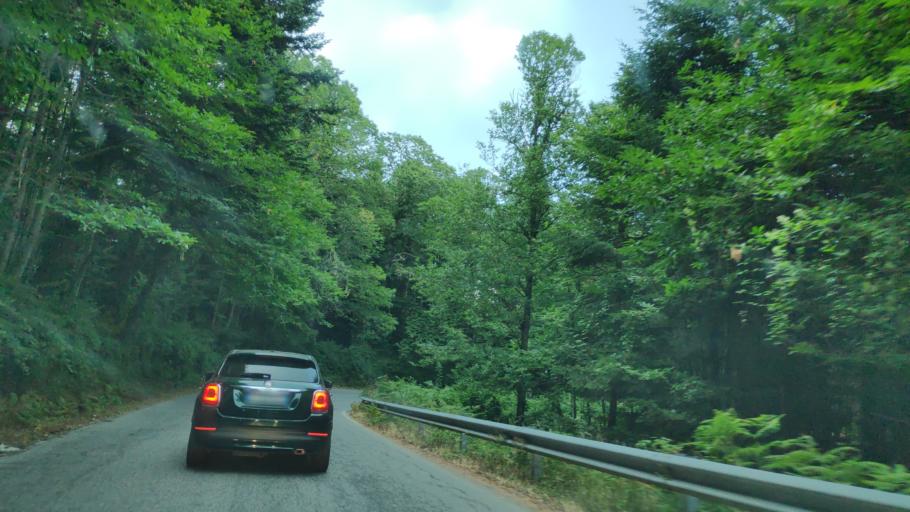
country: IT
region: Calabria
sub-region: Provincia di Vibo-Valentia
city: Serra San Bruno
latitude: 38.5515
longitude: 16.3223
